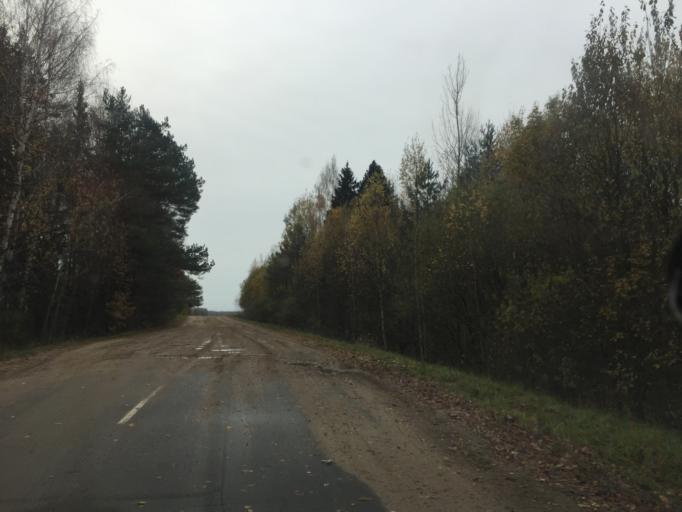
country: BY
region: Mogilev
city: Drybin
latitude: 54.0034
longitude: 31.0230
